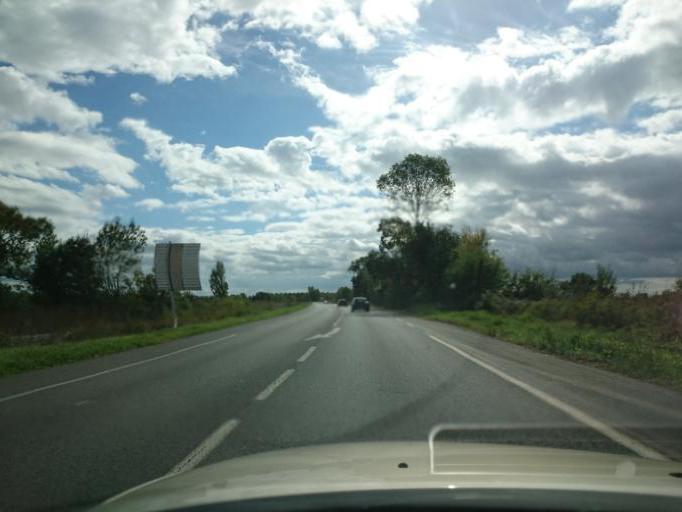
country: FR
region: Aquitaine
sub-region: Departement de la Gironde
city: Saint-Louis-de-Montferrand
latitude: 44.9423
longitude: -0.5608
